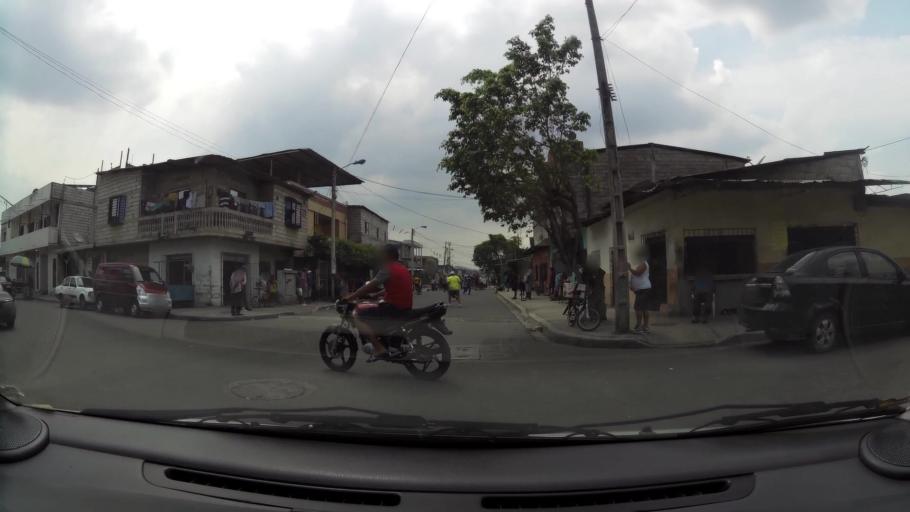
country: EC
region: Guayas
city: Guayaquil
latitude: -2.2368
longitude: -79.9187
